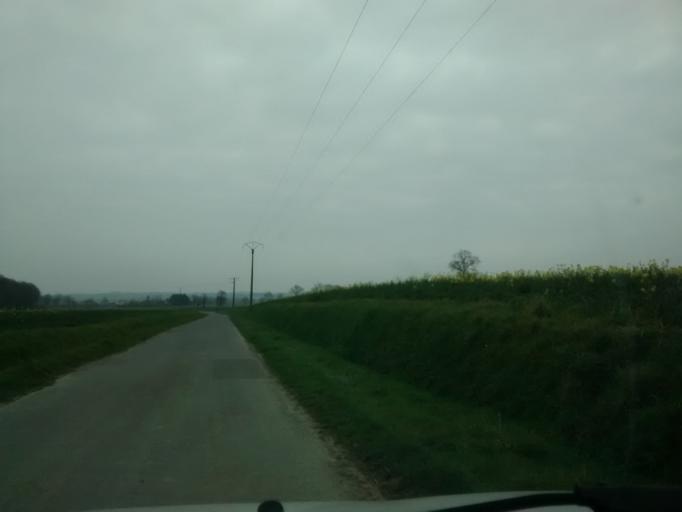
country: FR
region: Brittany
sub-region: Departement d'Ille-et-Vilaine
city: Bazouges-la-Perouse
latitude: 48.4063
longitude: -1.5479
